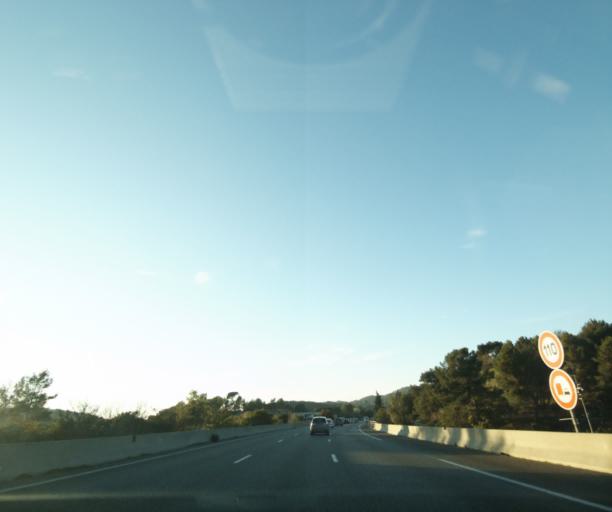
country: FR
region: Provence-Alpes-Cote d'Azur
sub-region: Departement des Bouches-du-Rhone
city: Le Tholonet
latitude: 43.5081
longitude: 5.5011
